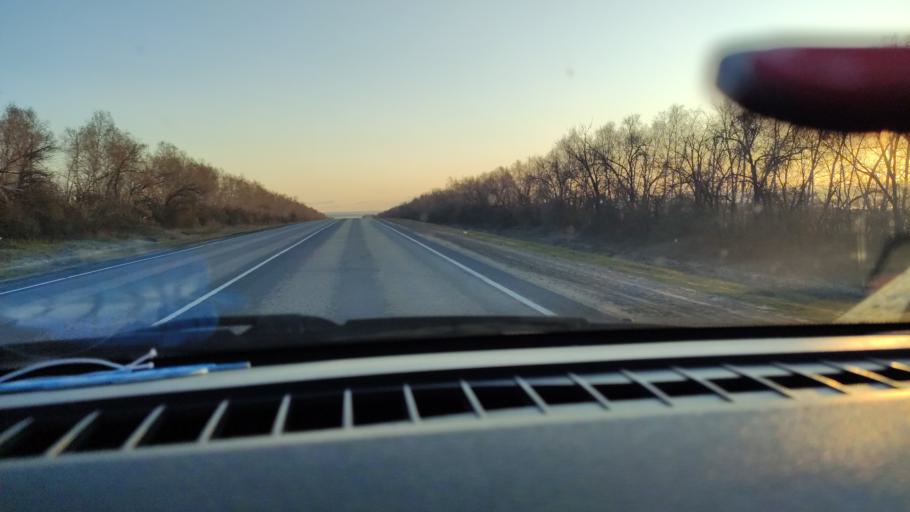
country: RU
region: Saratov
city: Sinodskoye
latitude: 51.9432
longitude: 46.5992
